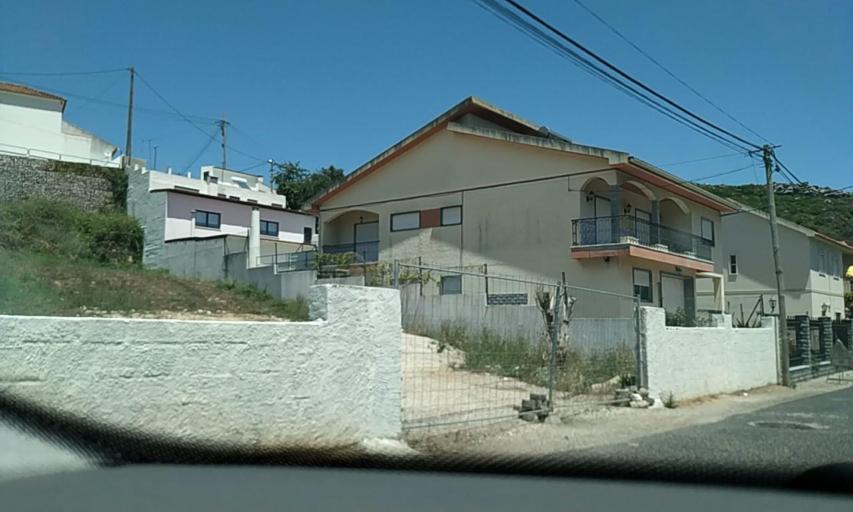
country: PT
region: Lisbon
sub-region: Odivelas
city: Canecas
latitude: 38.8667
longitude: -9.2137
